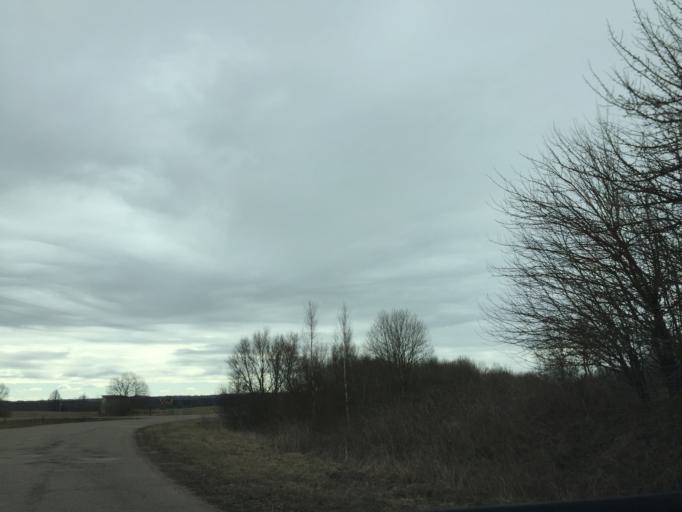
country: LV
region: Daugavpils
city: Daugavpils
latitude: 55.9152
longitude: 26.7486
